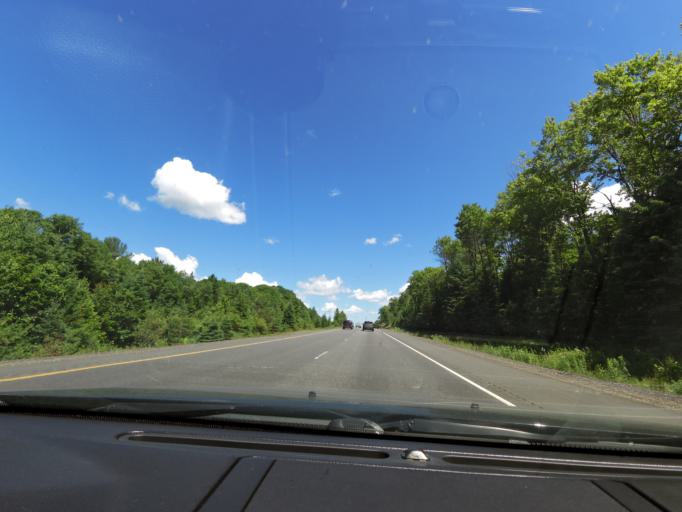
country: CA
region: Ontario
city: Bracebridge
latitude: 45.1849
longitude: -79.3123
